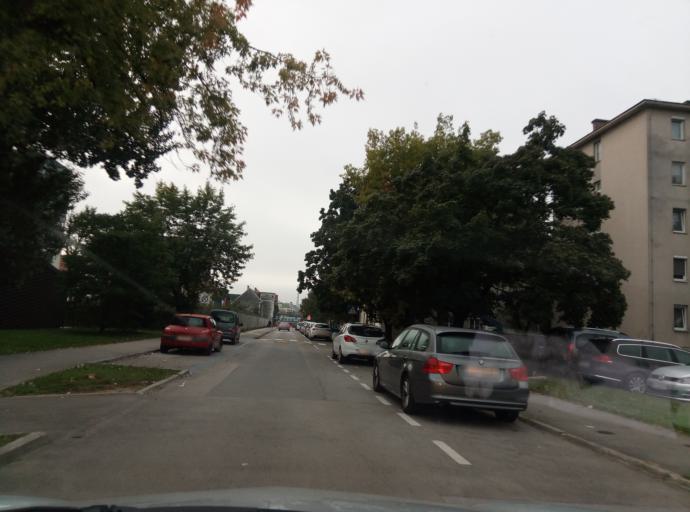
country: SI
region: Ljubljana
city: Ljubljana
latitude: 46.0619
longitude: 14.5178
